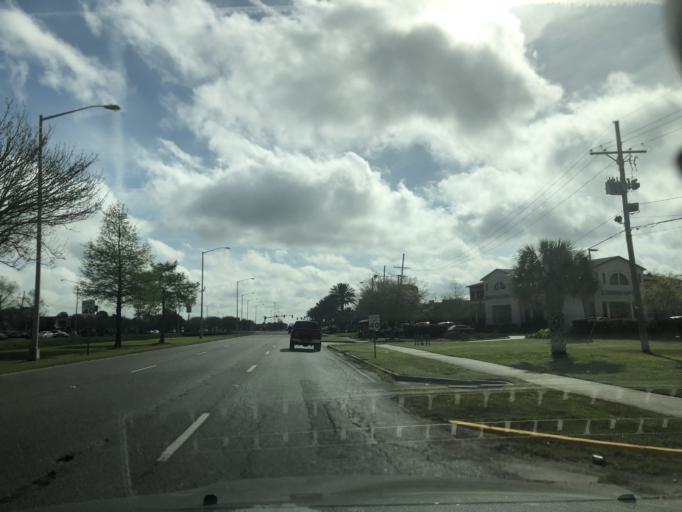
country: US
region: Louisiana
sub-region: Jefferson Parish
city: Metairie Terrace
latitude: 30.0054
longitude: -90.1937
